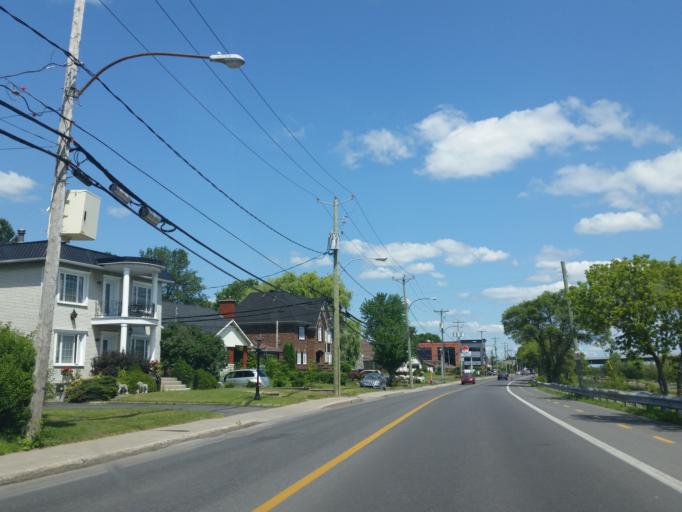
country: CA
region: Quebec
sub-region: Monteregie
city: Saint-Jean-sur-Richelieu
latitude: 45.3221
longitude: -73.2630
